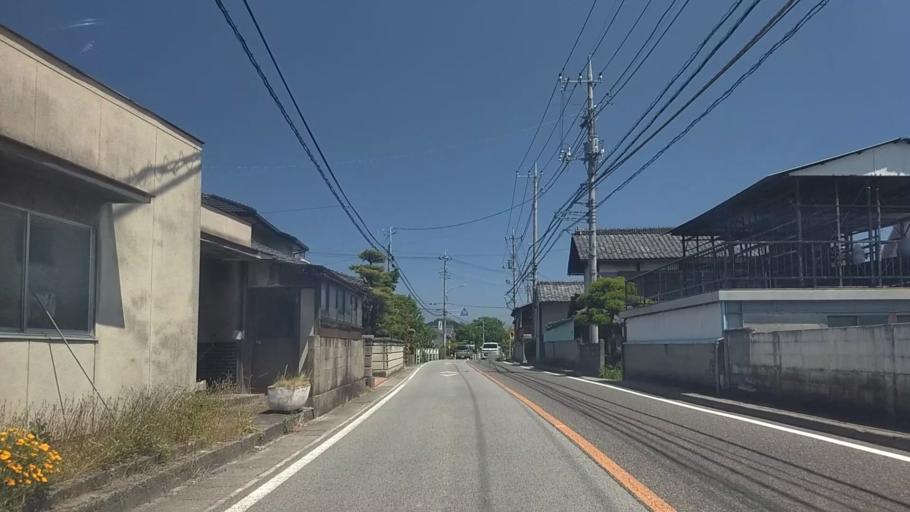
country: JP
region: Yamanashi
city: Ryuo
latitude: 35.6642
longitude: 138.4647
